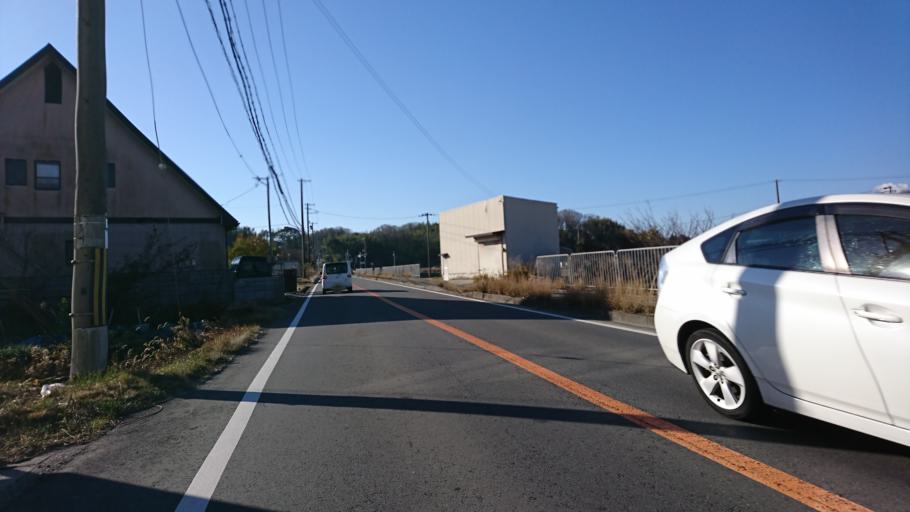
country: JP
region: Hyogo
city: Kakogawacho-honmachi
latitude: 34.8250
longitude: 134.8357
